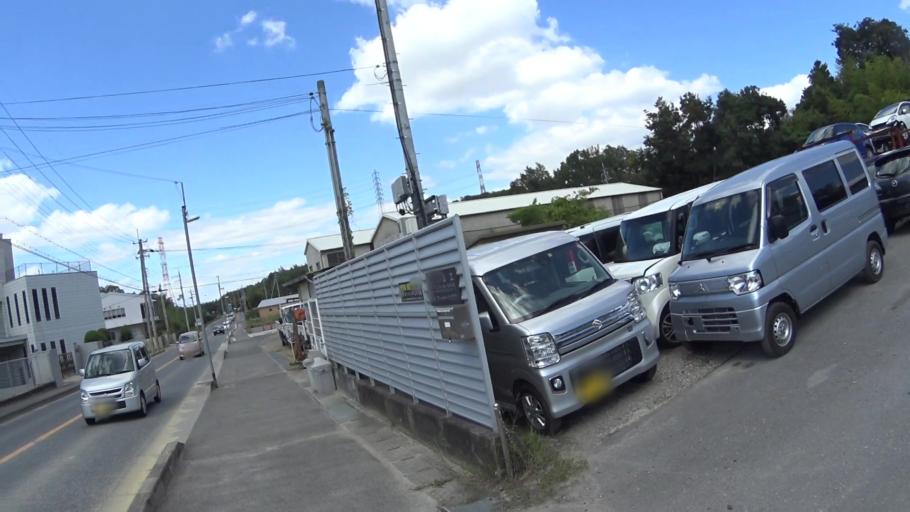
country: JP
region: Kyoto
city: Tanabe
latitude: 34.8443
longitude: 135.7925
